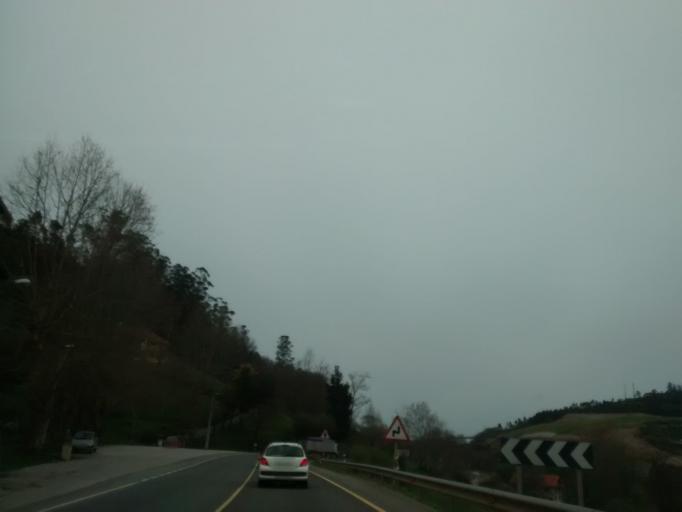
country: ES
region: Cantabria
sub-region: Provincia de Cantabria
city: Penagos
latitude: 43.3450
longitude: -3.7910
